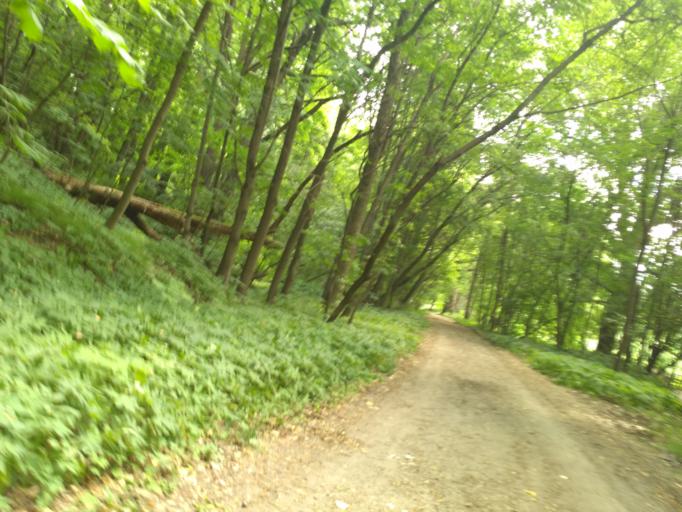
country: RU
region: Nizjnij Novgorod
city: Nizhniy Novgorod
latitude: 56.2590
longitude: 43.9702
